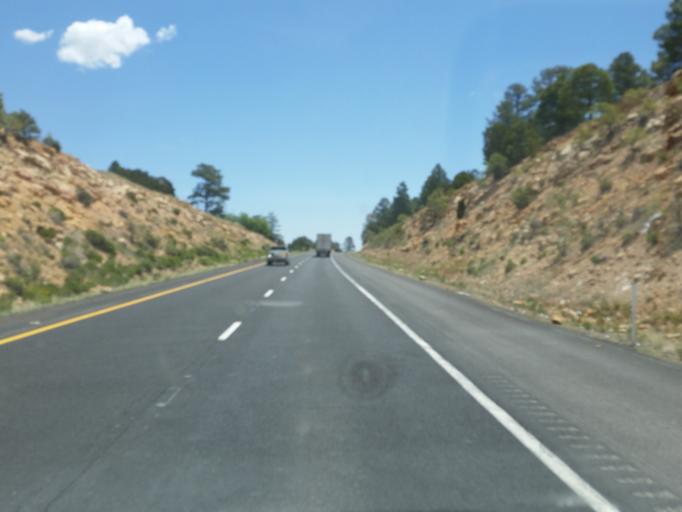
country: US
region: Arizona
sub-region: Coconino County
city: Flagstaff
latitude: 35.2183
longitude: -111.5667
